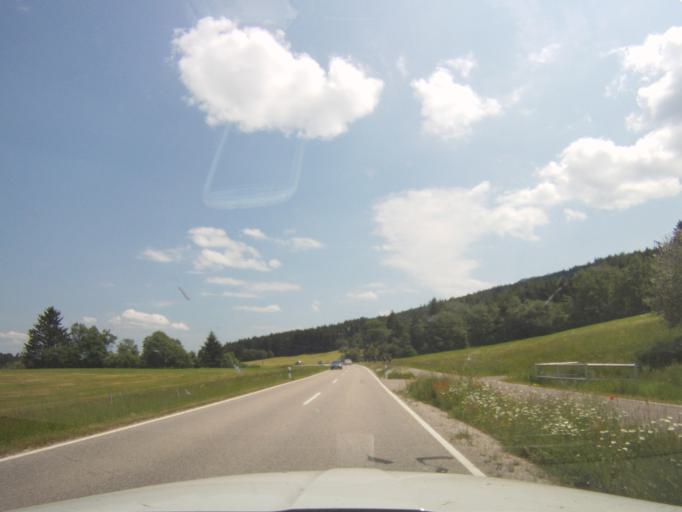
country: DE
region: Bavaria
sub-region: Swabia
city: Oy-Mittelberg
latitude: 47.6120
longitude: 10.4556
